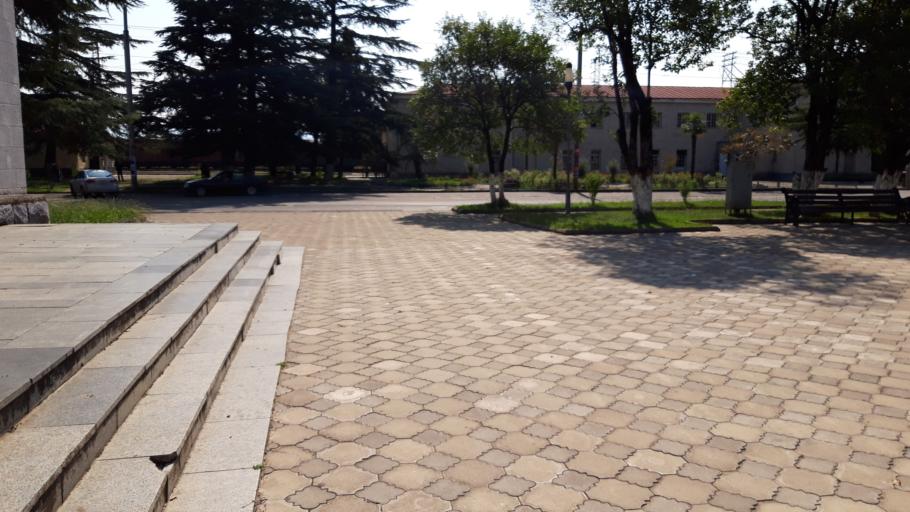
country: GE
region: Imereti
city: Samtredia
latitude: 42.1621
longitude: 42.3438
